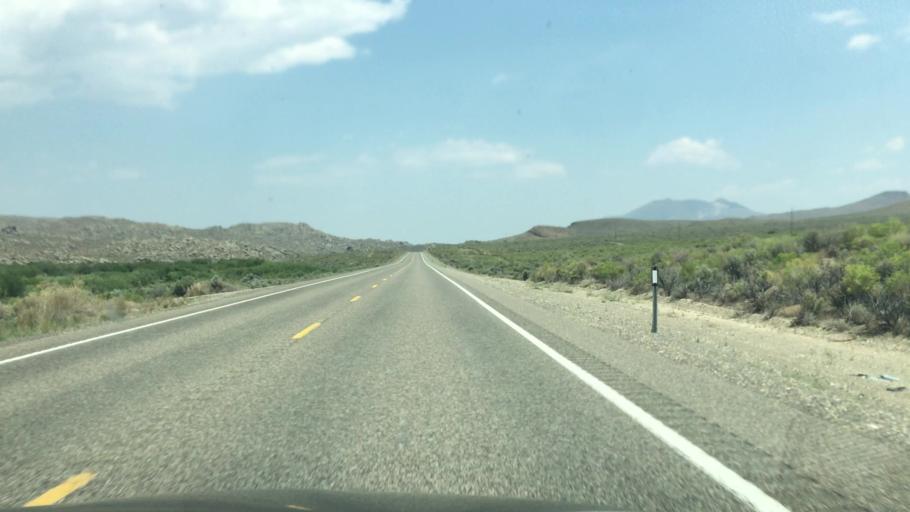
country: US
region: Nevada
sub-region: Elko County
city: Jackpot
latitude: 41.7265
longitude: -114.7970
